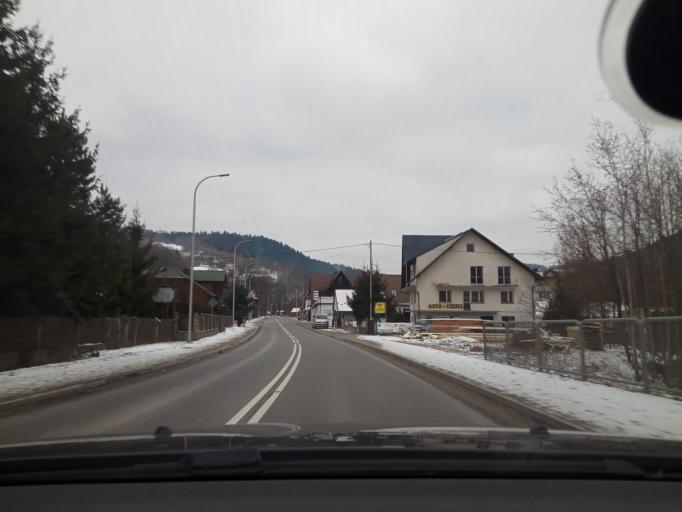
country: PL
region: Lesser Poland Voivodeship
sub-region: Powiat limanowski
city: Kamienica
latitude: 49.6018
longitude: 20.3003
